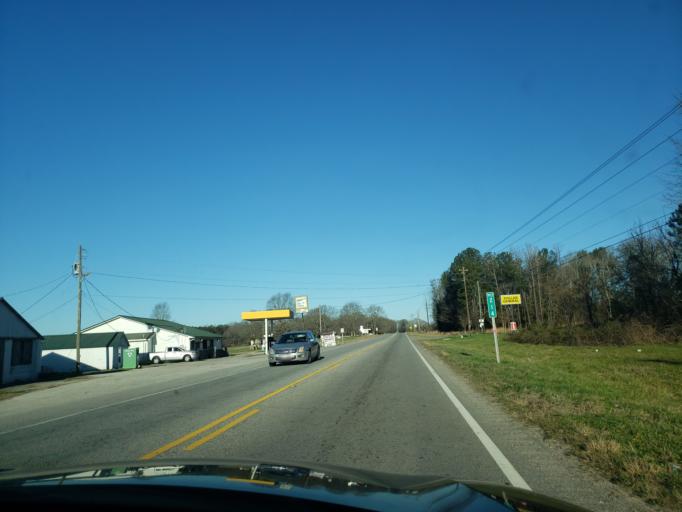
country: US
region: Alabama
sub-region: Lee County
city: Auburn
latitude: 32.5996
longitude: -85.5791
